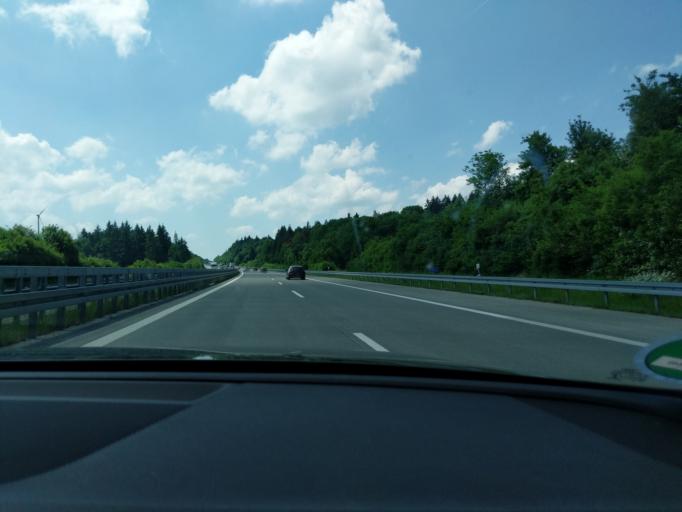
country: DE
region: Baden-Wuerttemberg
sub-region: Regierungsbezirk Stuttgart
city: Buch am Ahorn
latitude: 49.5270
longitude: 9.5738
